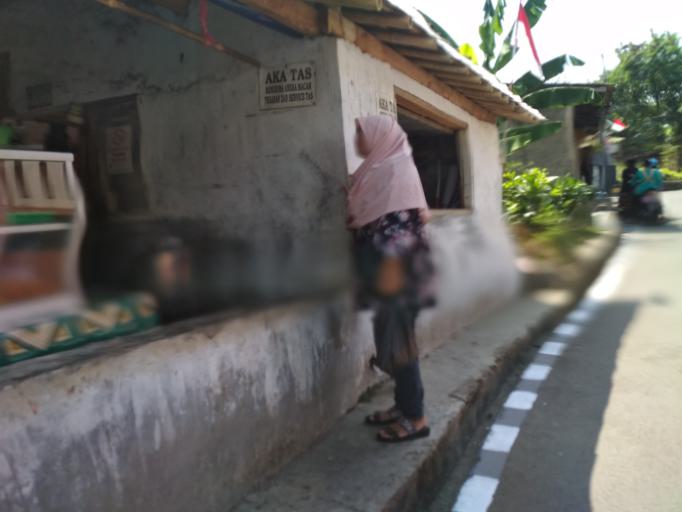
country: ID
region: West Java
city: Bogor
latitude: -6.5638
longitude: 106.7499
